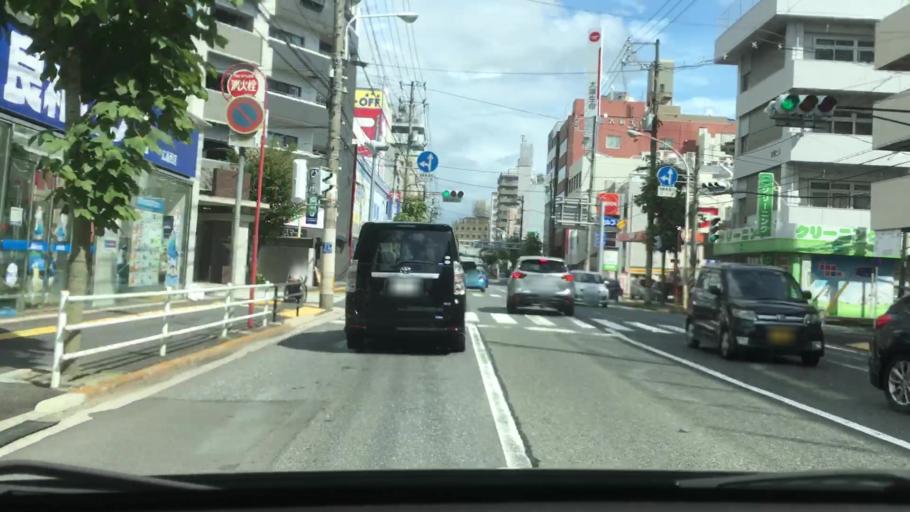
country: JP
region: Hiroshima
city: Hiroshima-shi
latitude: 34.3935
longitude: 132.4251
